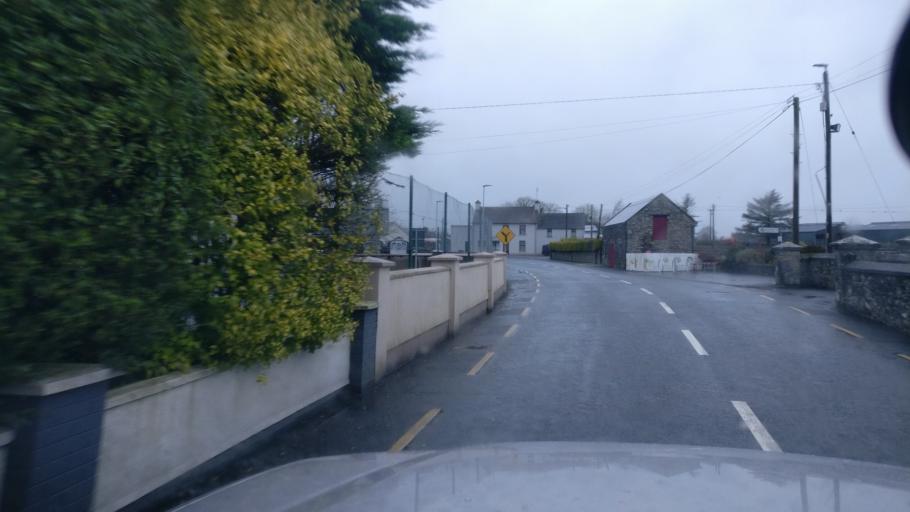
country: IE
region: Connaught
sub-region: County Galway
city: Portumna
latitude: 53.1023
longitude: -8.3927
